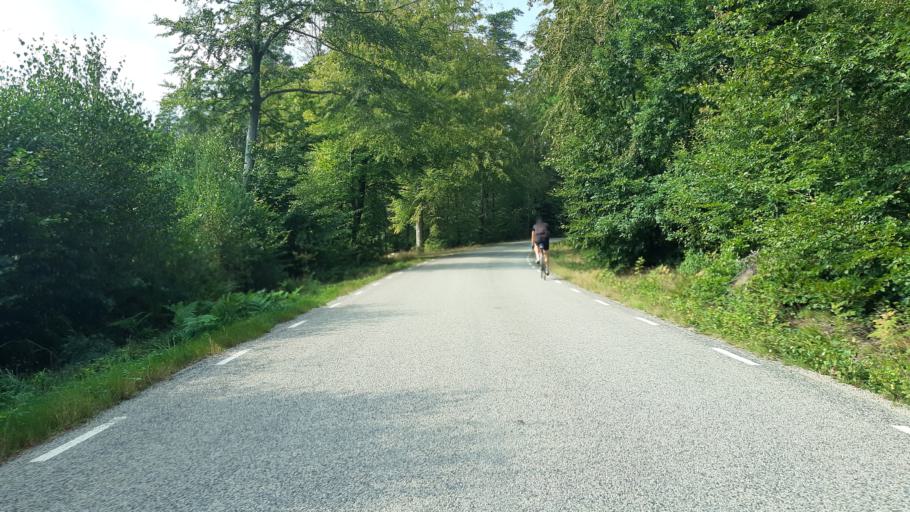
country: SE
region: Blekinge
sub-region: Karlskrona Kommun
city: Nattraby
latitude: 56.2127
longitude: 15.4601
